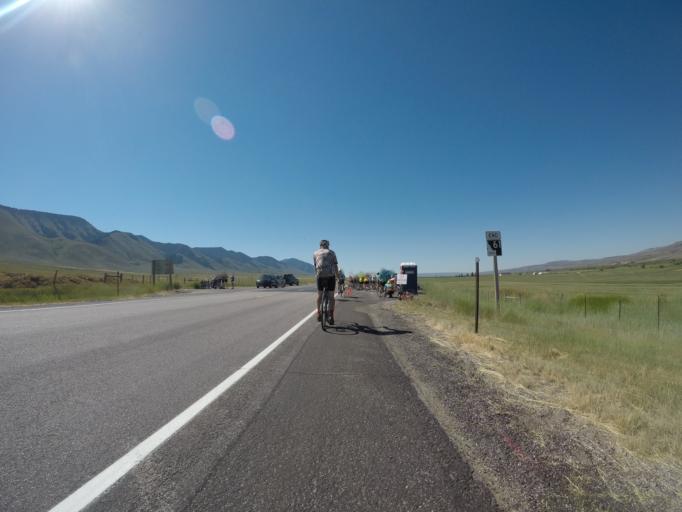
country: US
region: Idaho
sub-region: Bear Lake County
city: Montpelier
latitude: 42.3504
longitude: -111.0473
